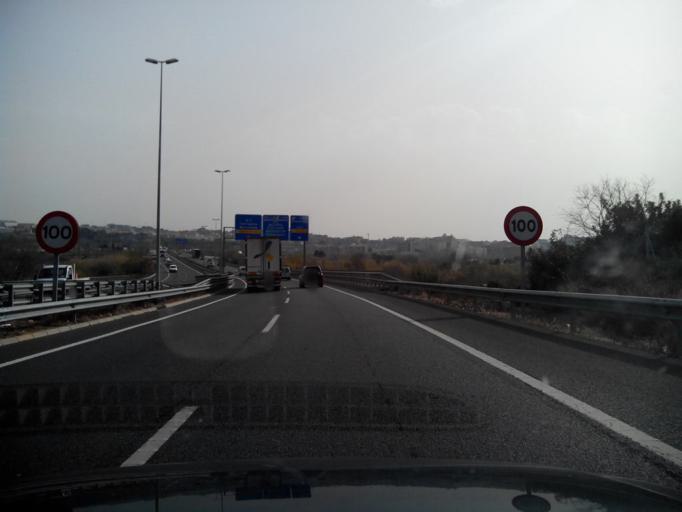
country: ES
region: Catalonia
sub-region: Provincia de Tarragona
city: Constanti
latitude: 41.1289
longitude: 1.2213
